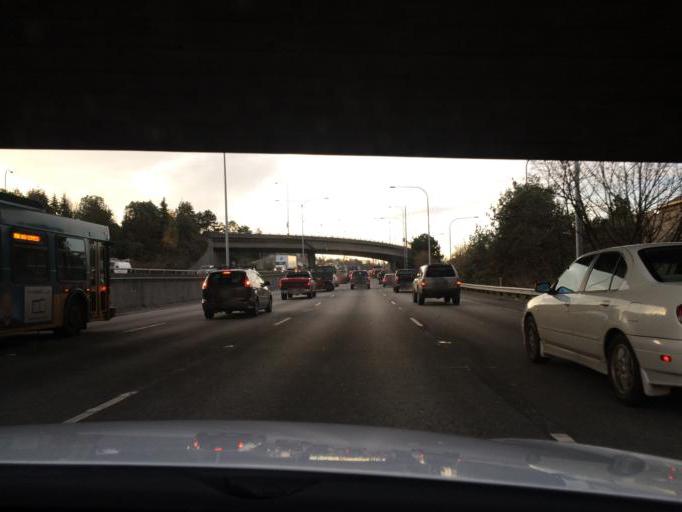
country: US
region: Washington
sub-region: King County
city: Seattle
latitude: 47.6434
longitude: -122.3228
